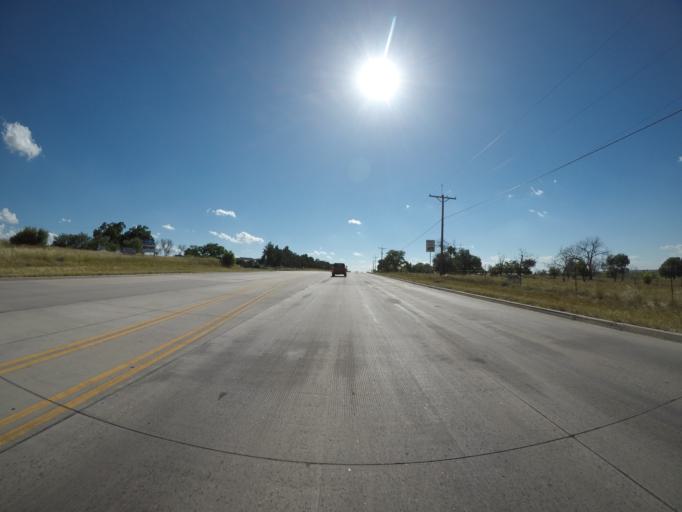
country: US
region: Colorado
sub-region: Logan County
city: Sterling
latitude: 40.6244
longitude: -103.2493
